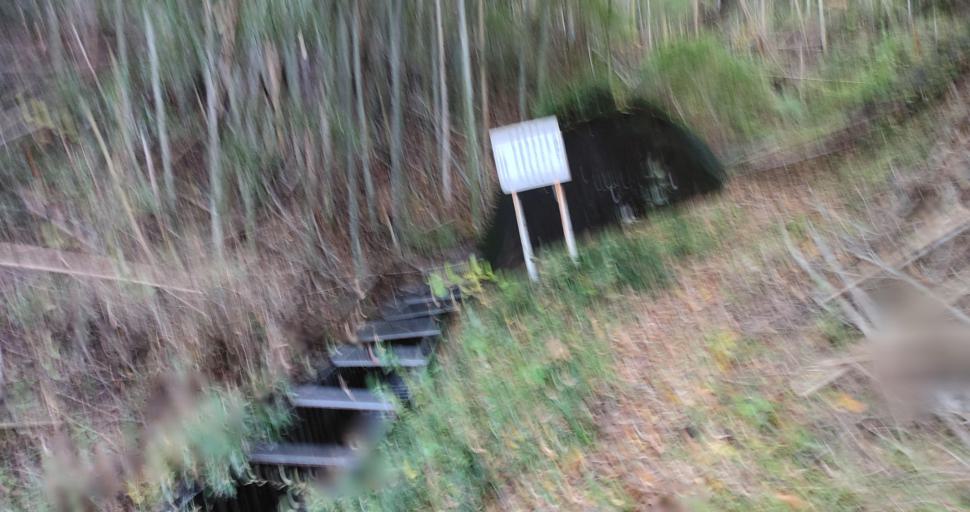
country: JP
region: Nagano
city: Kamimaruko
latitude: 36.3321
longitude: 138.3444
